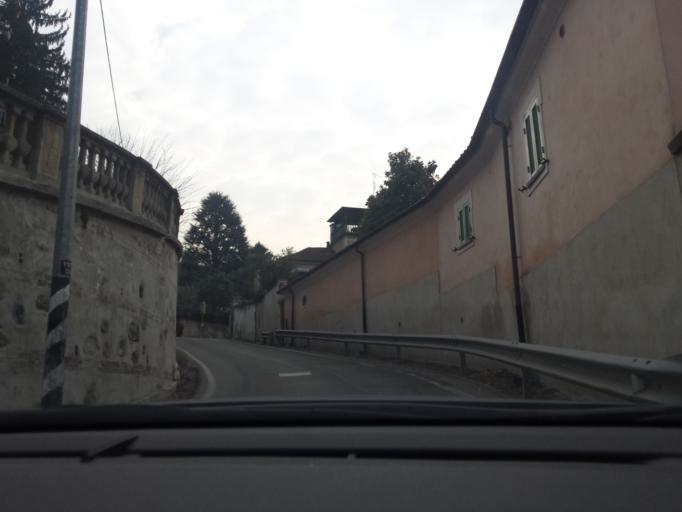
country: IT
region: Piedmont
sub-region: Provincia di Torino
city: Turin
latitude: 45.0588
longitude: 7.7186
